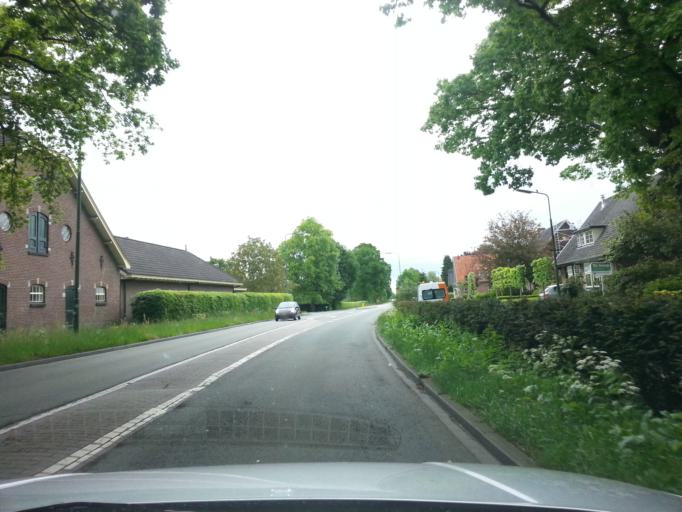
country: NL
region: Utrecht
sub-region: Gemeente Utrechtse Heuvelrug
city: Maarsbergen
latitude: 52.0603
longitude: 5.4038
